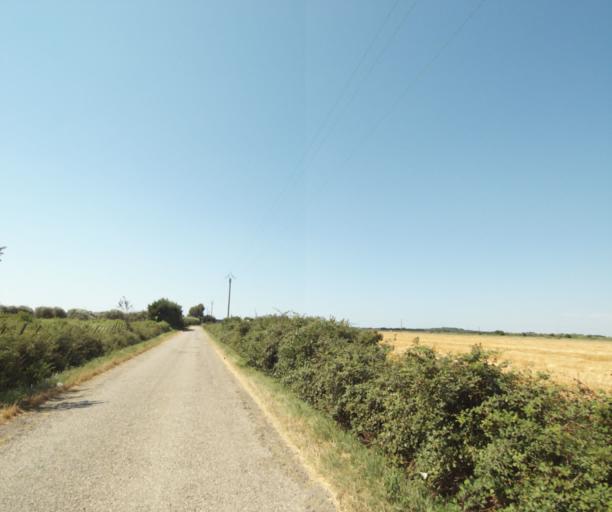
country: FR
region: Languedoc-Roussillon
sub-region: Departement de l'Herault
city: Marsillargues
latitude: 43.6521
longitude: 4.1637
